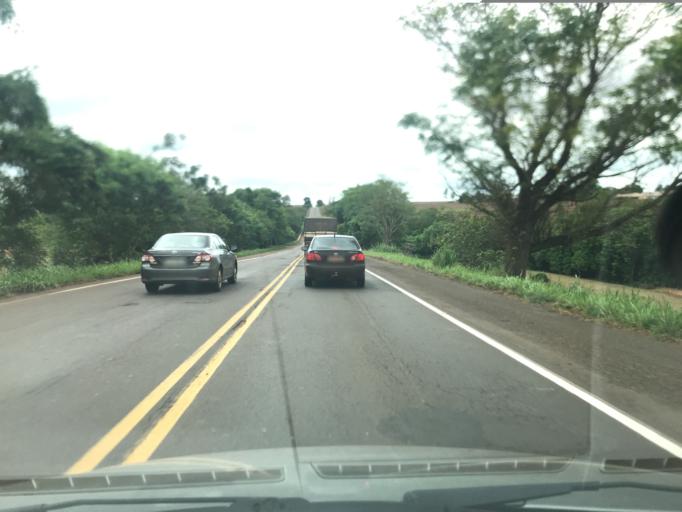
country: BR
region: Parana
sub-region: Terra Boa
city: Terra Boa
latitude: -23.6165
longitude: -52.4323
